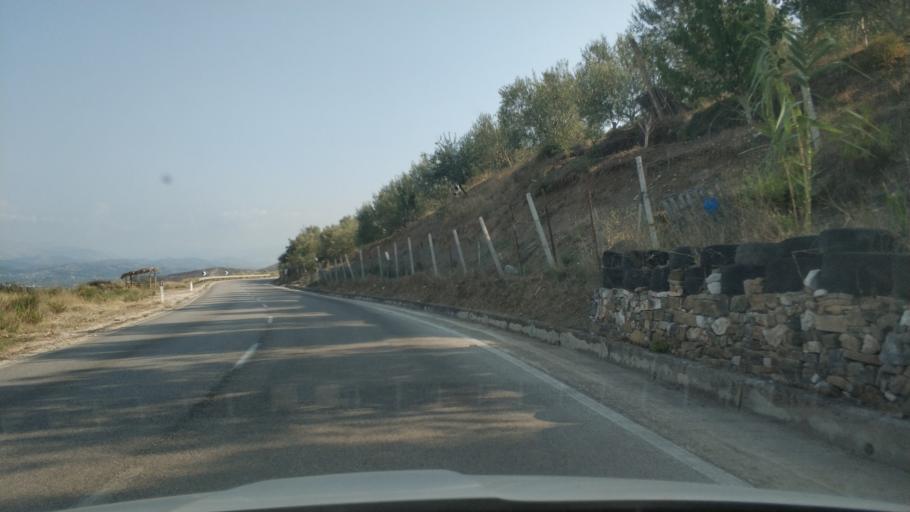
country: AL
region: Vlore
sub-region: Rrethi i Sarandes
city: Sarande
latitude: 39.8963
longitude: 20.0104
